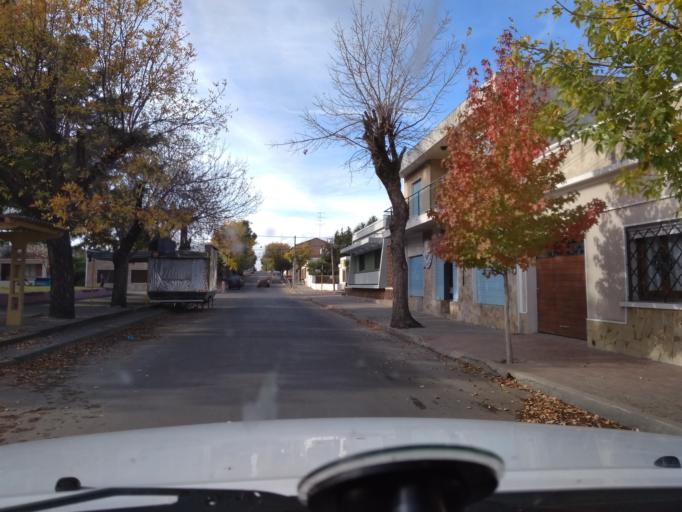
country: UY
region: Florida
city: Florida
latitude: -34.1001
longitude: -56.2198
